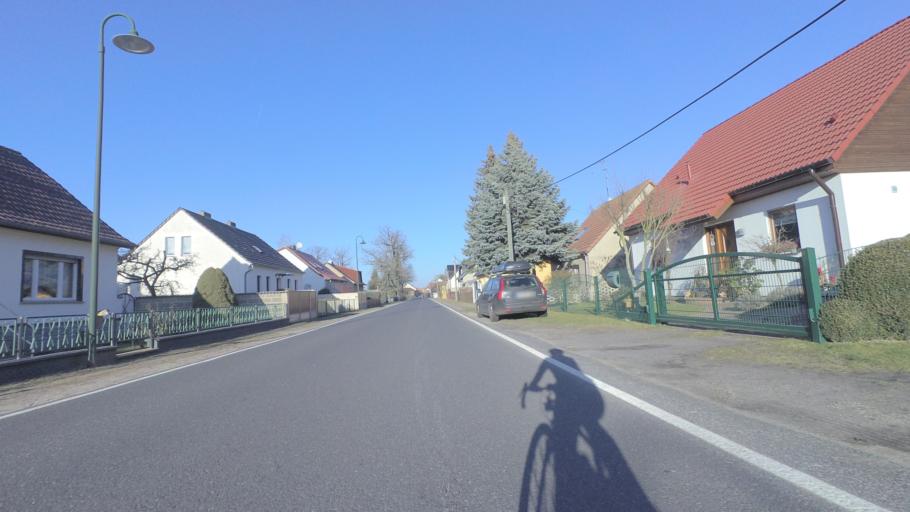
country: DE
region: Brandenburg
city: Sperenberg
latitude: 52.0407
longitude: 13.3201
